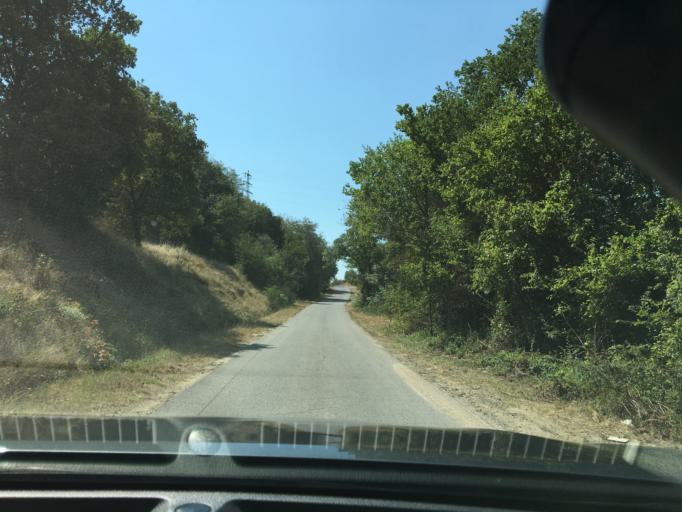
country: BG
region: Kyustendil
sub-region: Obshtina Rila
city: Rila
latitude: 42.1420
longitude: 23.0930
